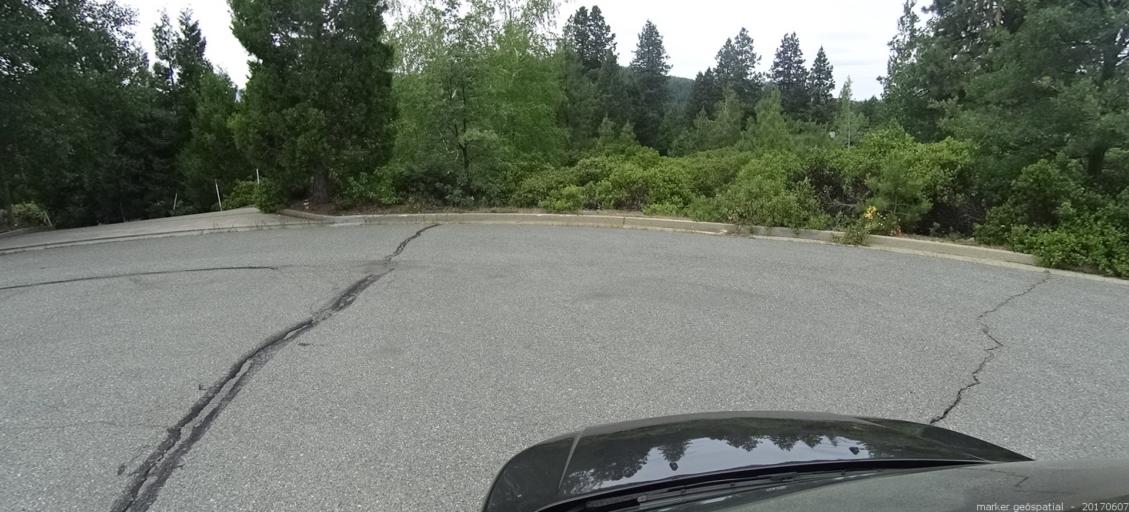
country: US
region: California
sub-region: Siskiyou County
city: Mount Shasta
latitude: 41.2881
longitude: -122.3170
